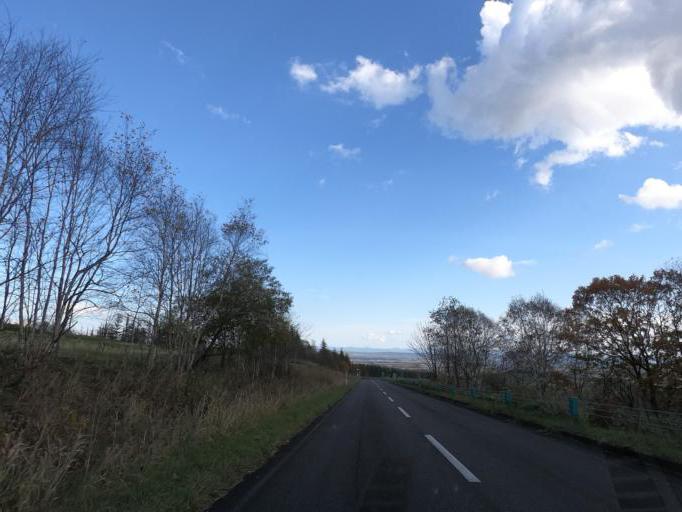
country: JP
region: Hokkaido
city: Otofuke
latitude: 43.2907
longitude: 143.2068
